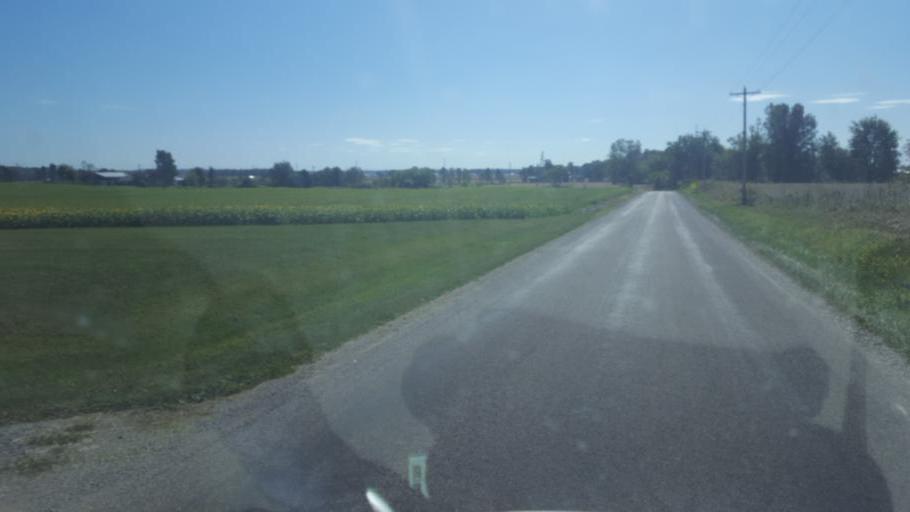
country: US
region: Ohio
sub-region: Huron County
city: Willard
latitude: 40.9481
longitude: -82.8349
